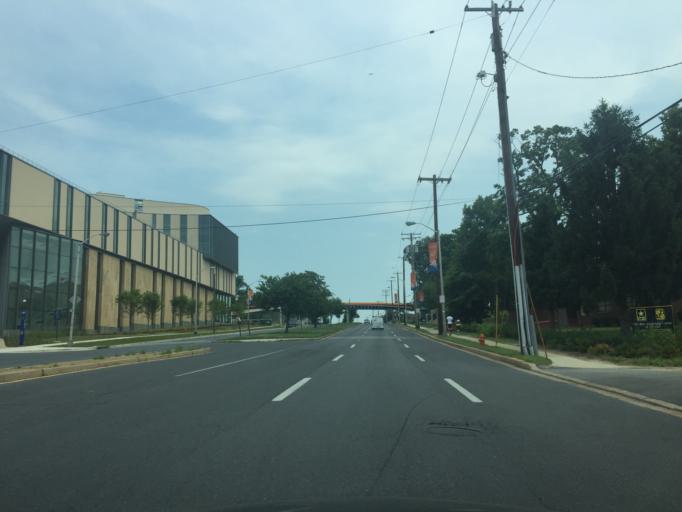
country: US
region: Maryland
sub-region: City of Baltimore
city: Baltimore
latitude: 39.3400
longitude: -76.5878
